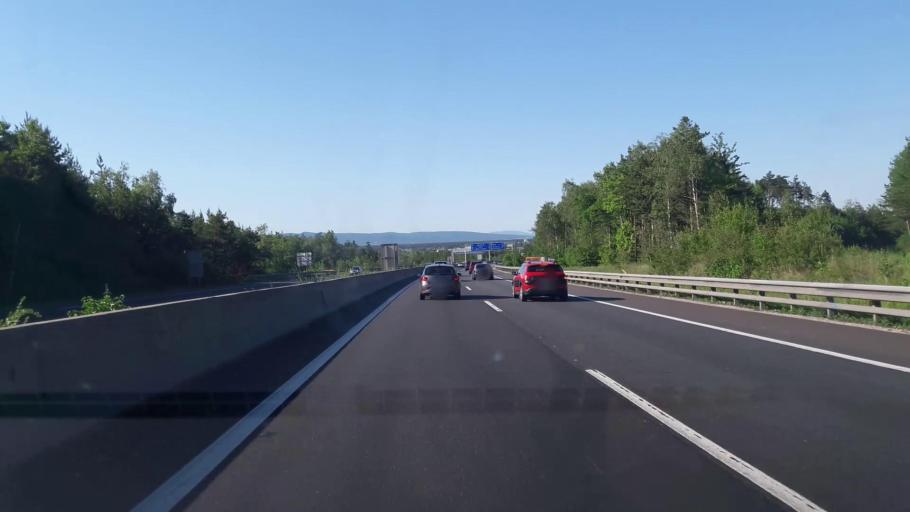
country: AT
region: Lower Austria
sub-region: Politischer Bezirk Neunkirchen
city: Seebenstein
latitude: 47.7093
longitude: 16.1294
